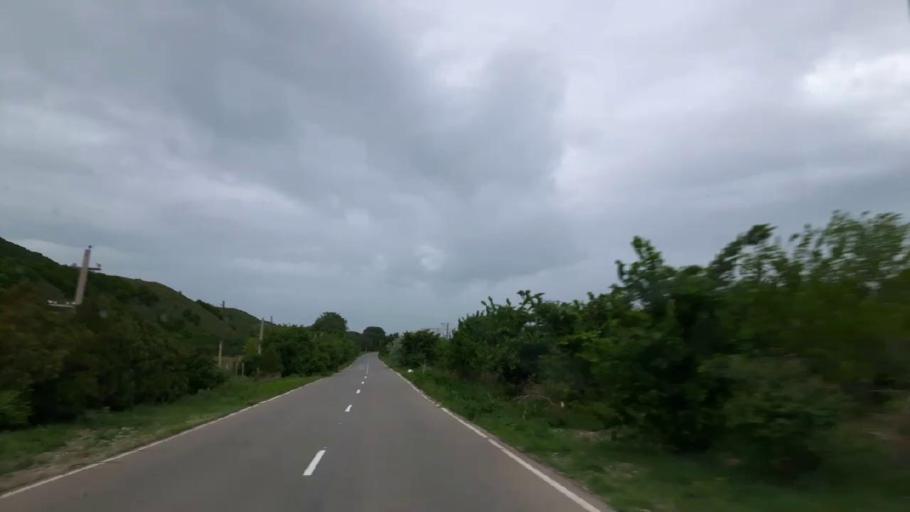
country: GE
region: Shida Kartli
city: Gori
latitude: 41.9932
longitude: 44.0307
